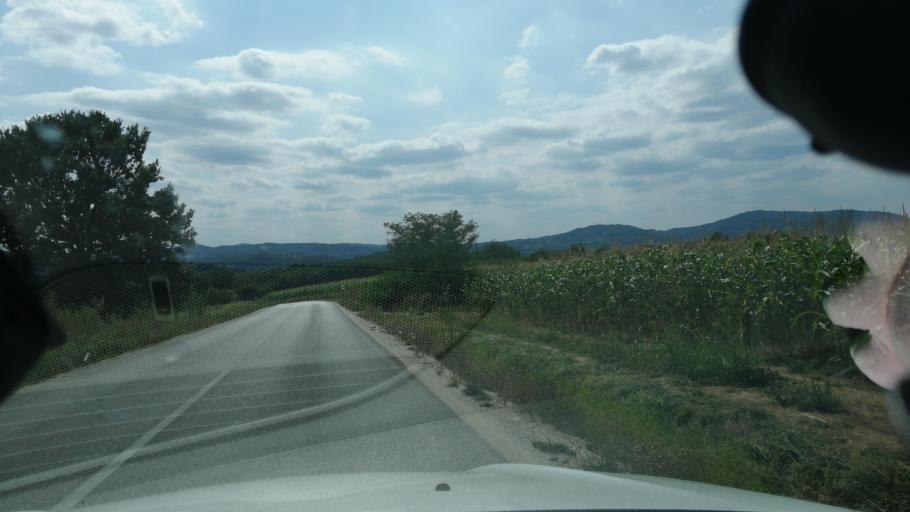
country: RS
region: Central Serbia
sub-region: Moravicki Okrug
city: Cacak
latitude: 43.8080
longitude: 20.2700
